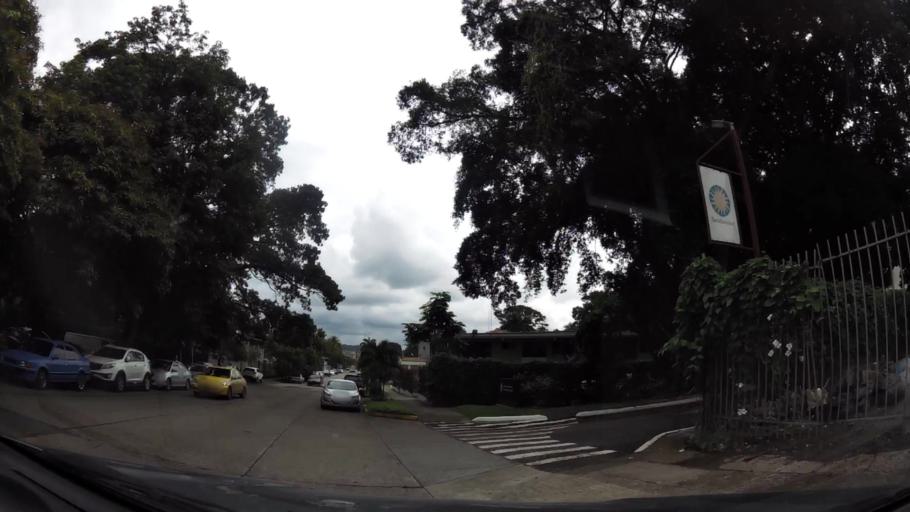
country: PA
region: Panama
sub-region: Distrito de Panama
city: Ancon
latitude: 8.9620
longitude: -79.5446
